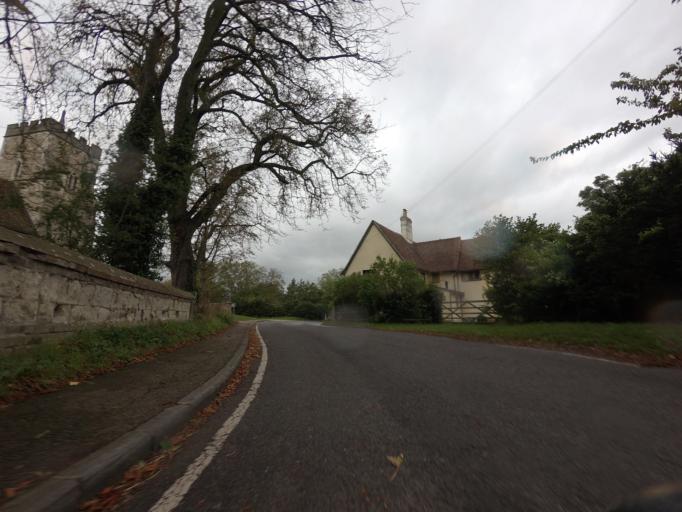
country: GB
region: England
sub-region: Cambridgeshire
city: Comberton
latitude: 52.1616
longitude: -0.0032
